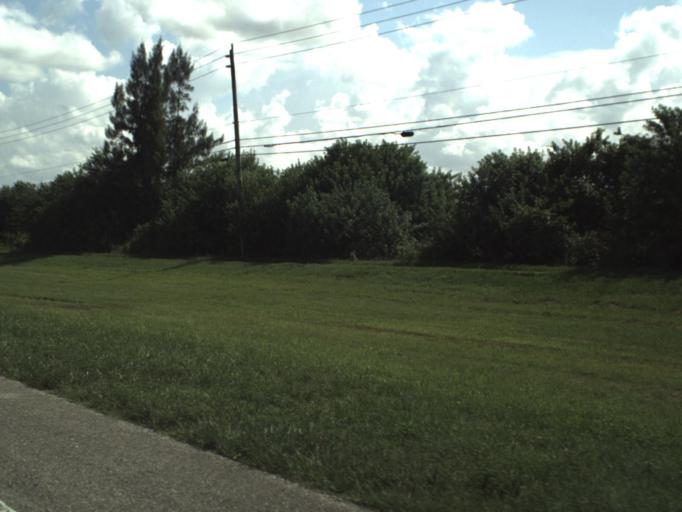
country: US
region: Florida
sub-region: Palm Beach County
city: Villages of Oriole
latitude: 26.4590
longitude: -80.2047
